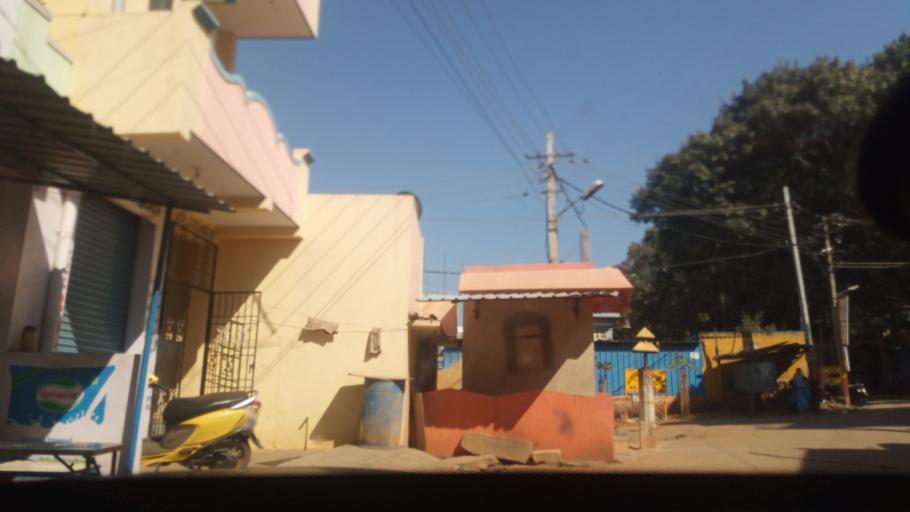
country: IN
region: Karnataka
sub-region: Bangalore Rural
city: Nelamangala
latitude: 13.0407
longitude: 77.4960
